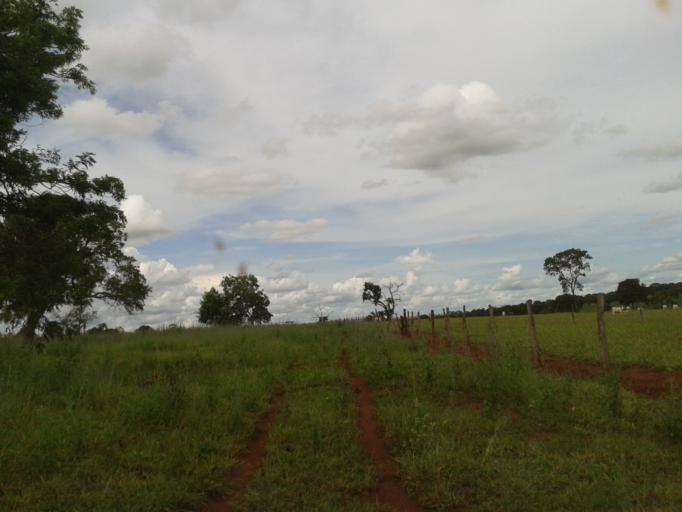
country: BR
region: Minas Gerais
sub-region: Santa Vitoria
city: Santa Vitoria
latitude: -18.7995
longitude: -49.8492
